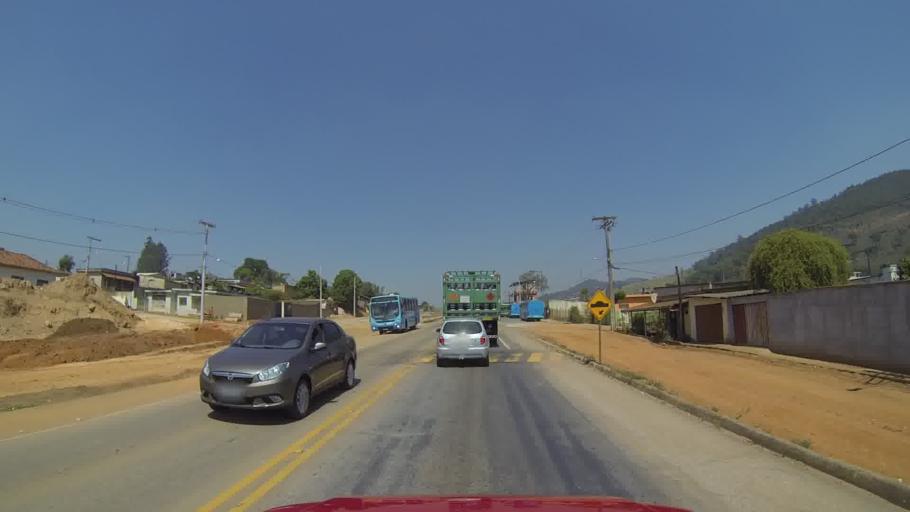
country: BR
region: Minas Gerais
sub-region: Mateus Leme
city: Mateus Leme
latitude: -20.0120
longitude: -44.4769
